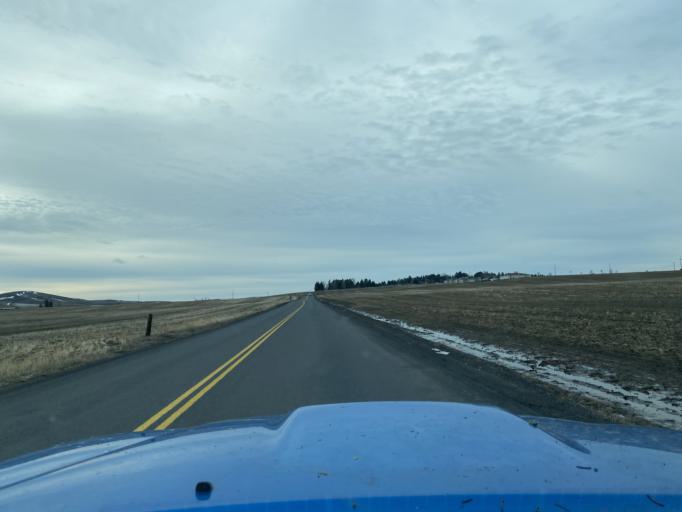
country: US
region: Idaho
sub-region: Latah County
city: Moscow
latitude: 46.7156
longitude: -116.9732
